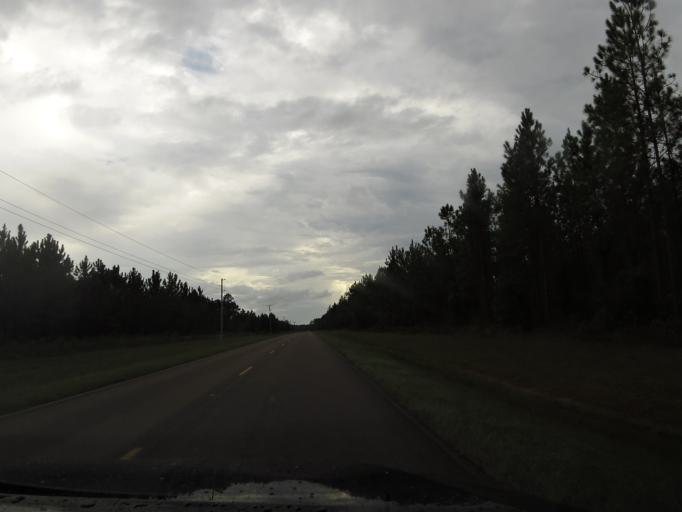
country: US
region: Florida
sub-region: Nassau County
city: Callahan
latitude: 30.5160
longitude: -81.9931
